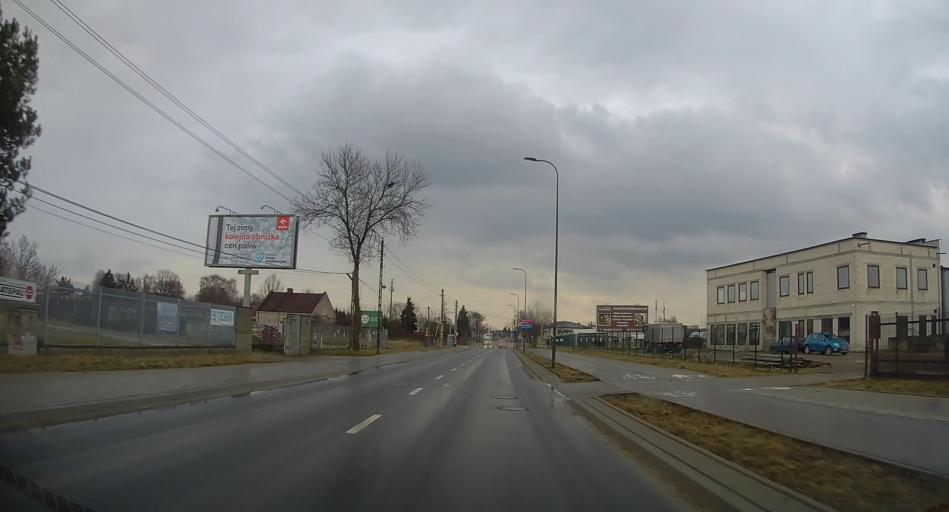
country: PL
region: Masovian Voivodeship
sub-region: Warszawa
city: Wawer
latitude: 52.1953
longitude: 21.1371
